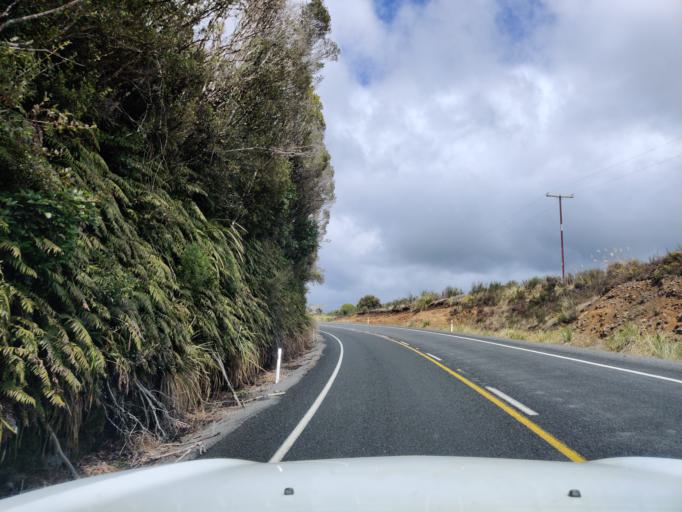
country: NZ
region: Manawatu-Wanganui
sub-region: Ruapehu District
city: Waiouru
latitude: -39.2793
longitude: 175.3864
